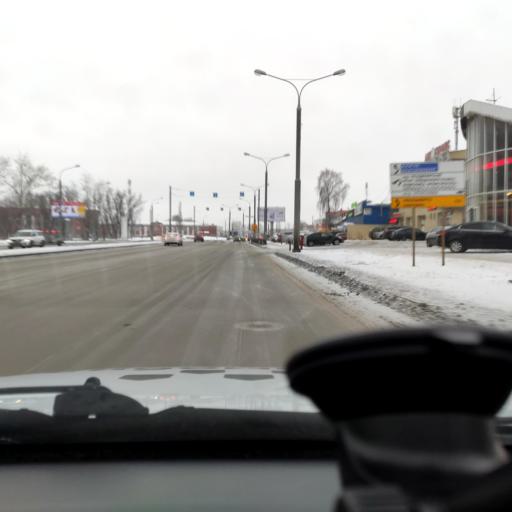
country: RU
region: Perm
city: Perm
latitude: 57.9690
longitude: 56.2614
